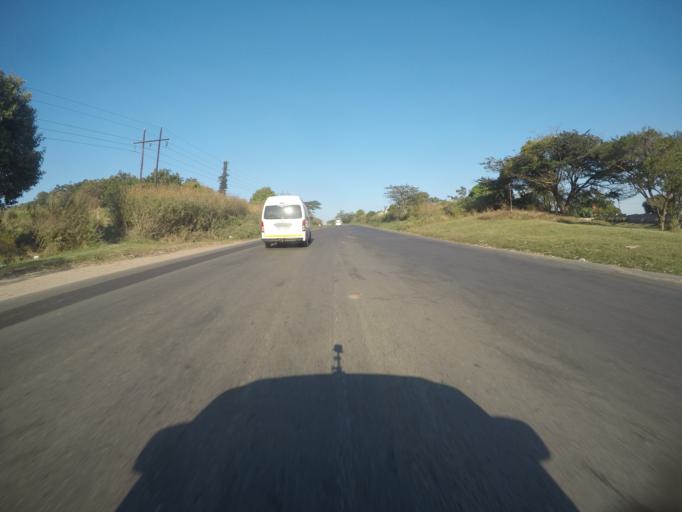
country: ZA
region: KwaZulu-Natal
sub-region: iLembe District Municipality
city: Stanger
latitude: -29.3868
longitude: 31.2528
